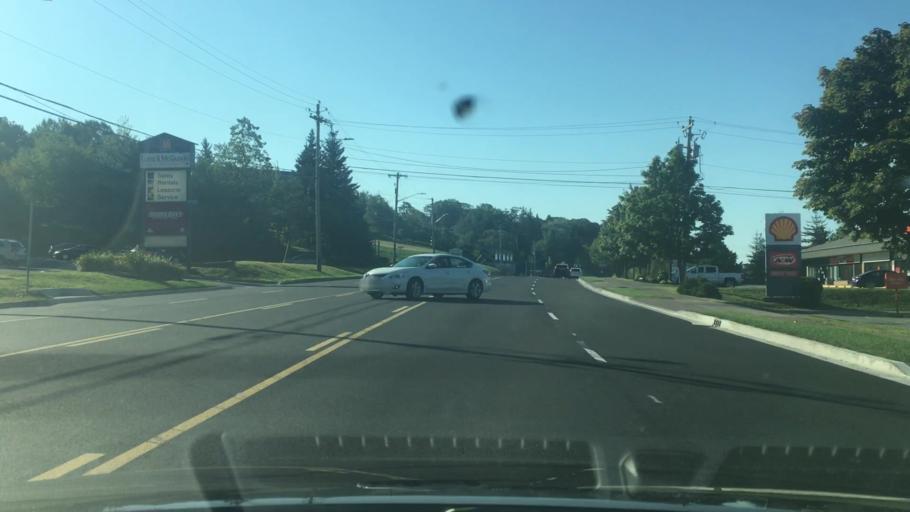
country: CA
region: Nova Scotia
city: Dartmouth
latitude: 44.7397
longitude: -63.6546
